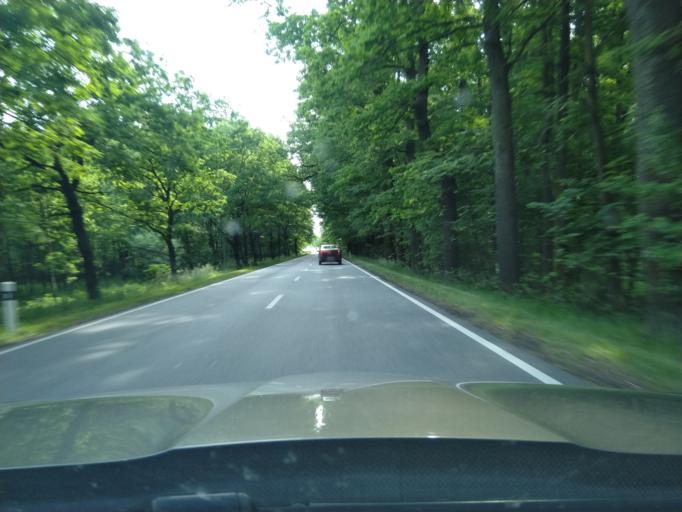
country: CZ
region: Jihocesky
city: Zliv
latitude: 49.0332
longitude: 14.3461
